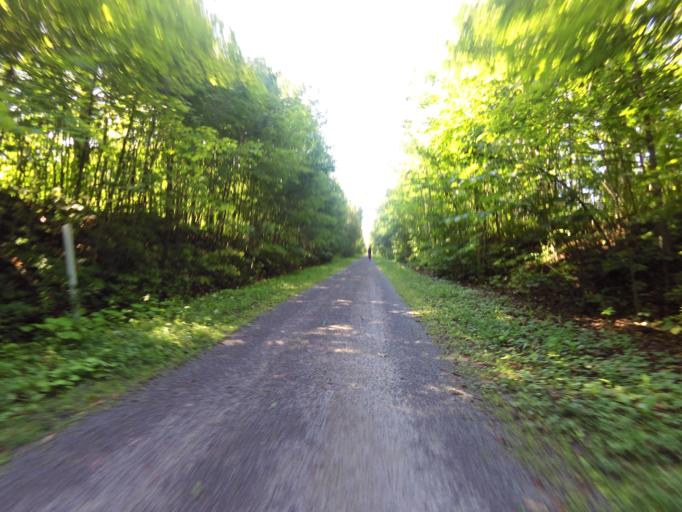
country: CA
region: Ontario
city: Ottawa
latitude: 45.2237
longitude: -75.6212
